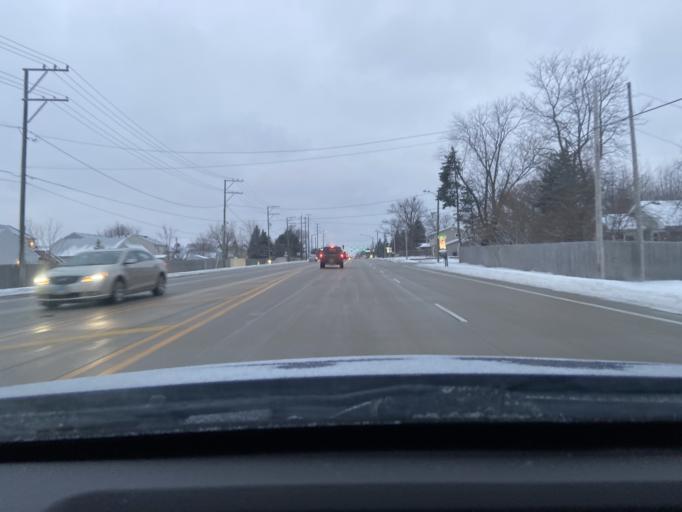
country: US
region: Illinois
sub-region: Lake County
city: Round Lake Park
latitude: 42.3571
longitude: -88.0649
